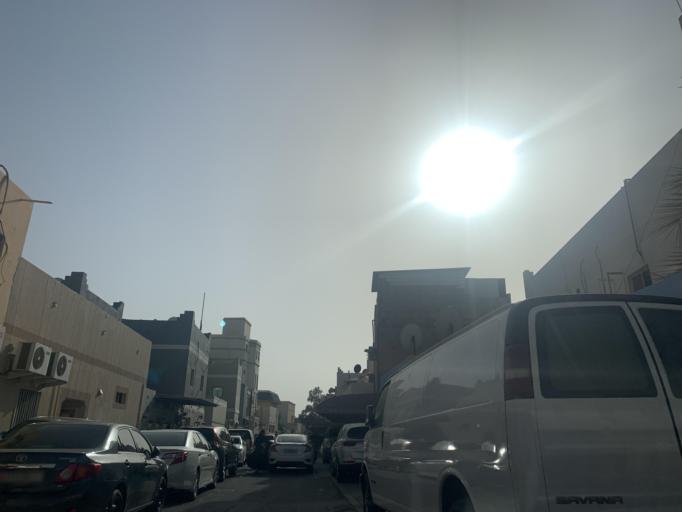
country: BH
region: Manama
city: Jidd Hafs
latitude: 26.2269
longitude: 50.5486
